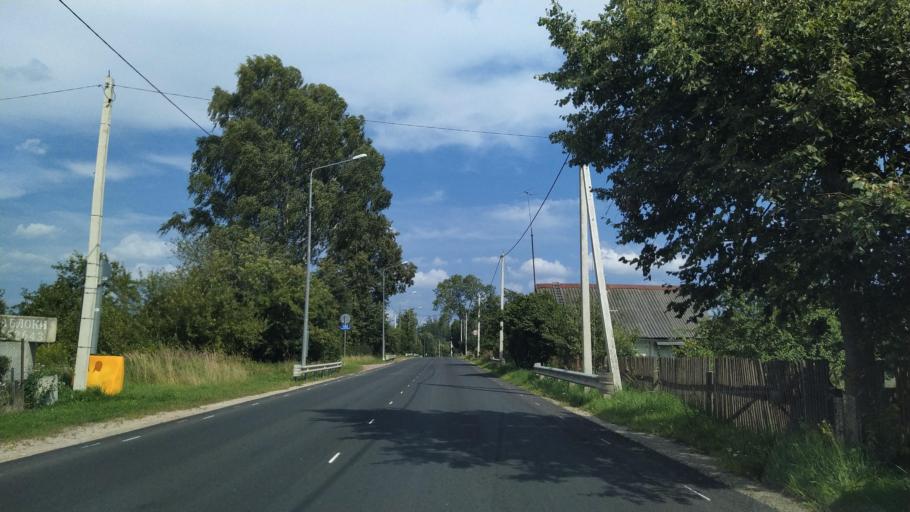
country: RU
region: Pskov
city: Porkhov
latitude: 57.7431
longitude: 29.0381
